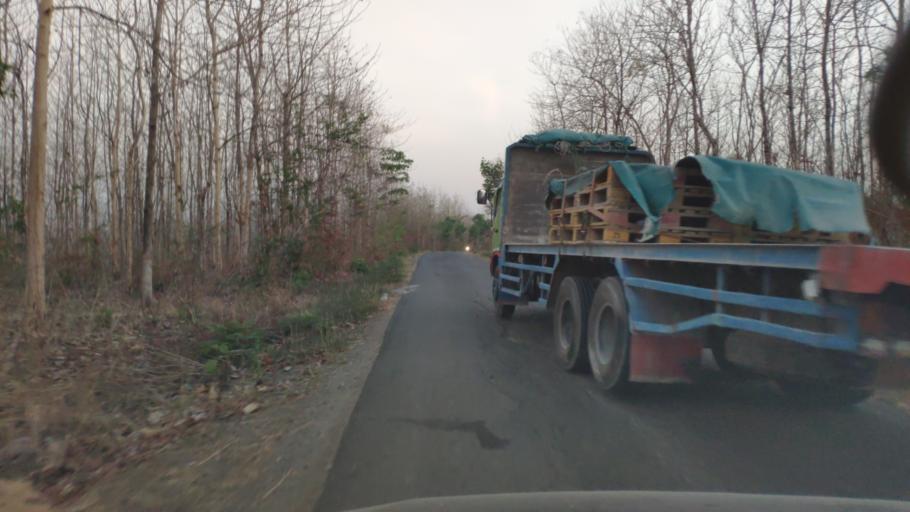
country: ID
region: Central Java
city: Ngliron
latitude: -7.1290
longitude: 111.4226
